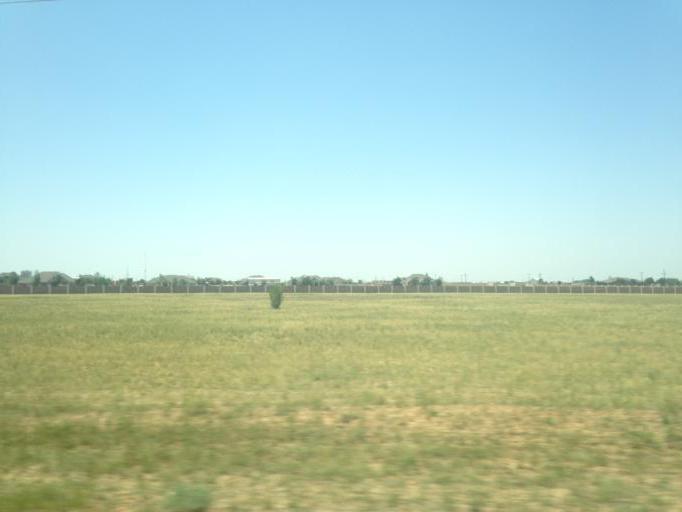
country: US
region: Texas
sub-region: Midland County
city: Midland
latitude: 32.0572
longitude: -102.0282
